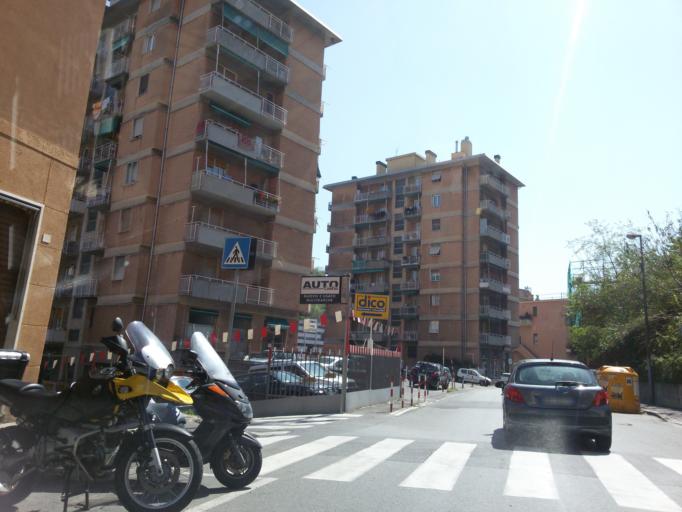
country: IT
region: Liguria
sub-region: Provincia di Genova
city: Piccarello
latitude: 44.4501
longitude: 8.9722
